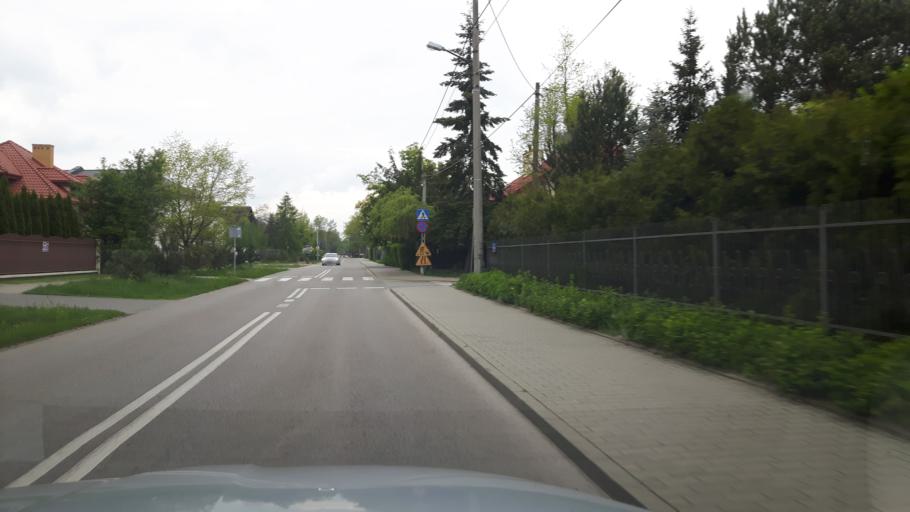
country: PL
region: Masovian Voivodeship
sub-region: Warszawa
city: Rembertow
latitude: 52.2698
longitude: 21.1617
